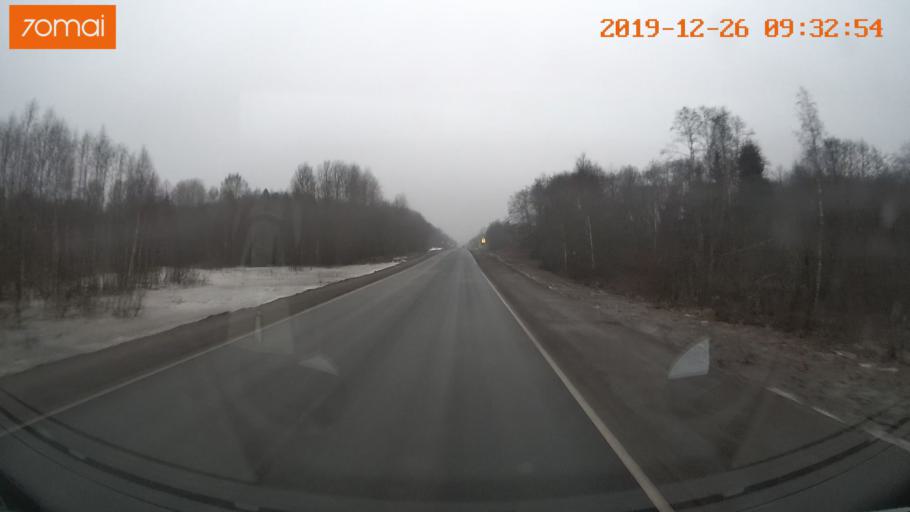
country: RU
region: Vologda
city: Gryazovets
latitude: 59.0835
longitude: 40.1091
